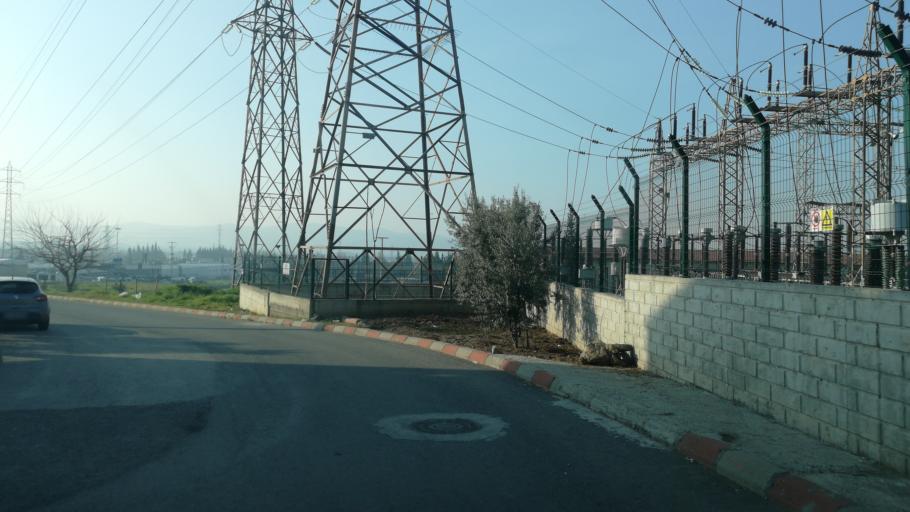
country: TR
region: Kahramanmaras
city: Kahramanmaras
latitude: 37.5664
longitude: 36.9435
